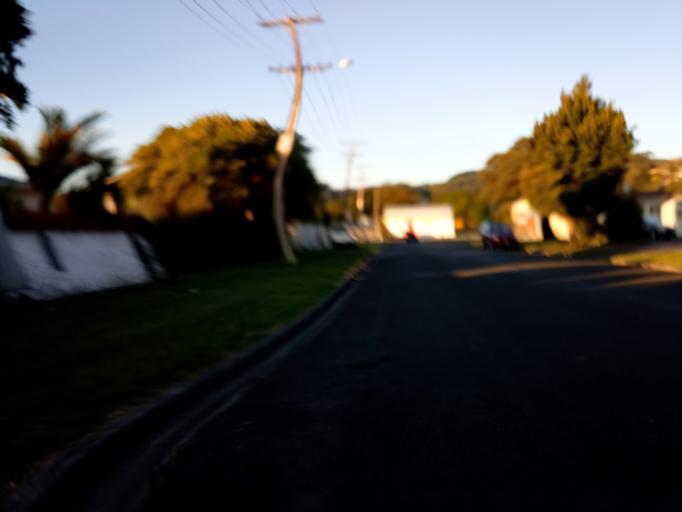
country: NZ
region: Gisborne
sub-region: Gisborne District
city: Gisborne
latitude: -38.6439
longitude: 178.0092
